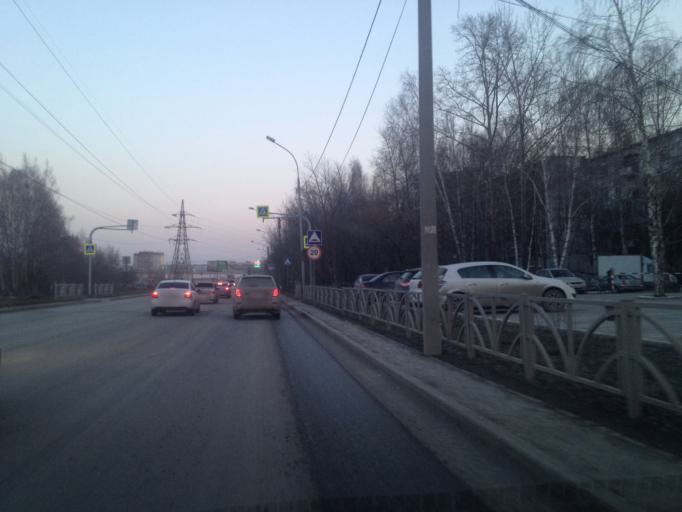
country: RU
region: Sverdlovsk
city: Sovkhoznyy
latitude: 56.7764
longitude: 60.5987
